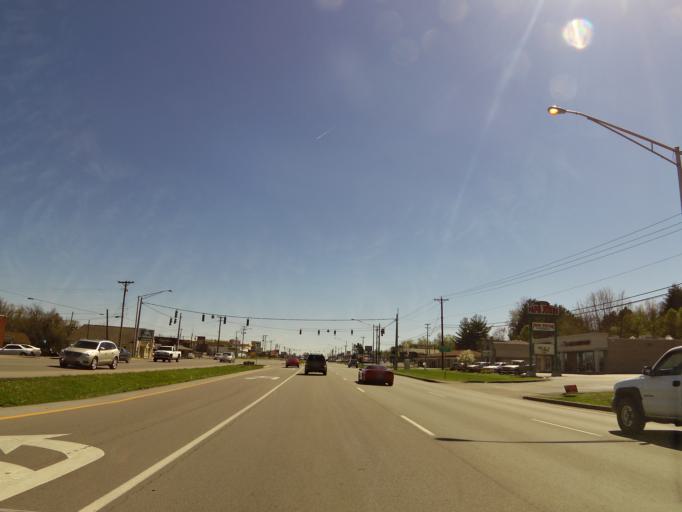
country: US
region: Kentucky
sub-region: Pulaski County
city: Somerset
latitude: 37.0828
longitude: -84.6170
